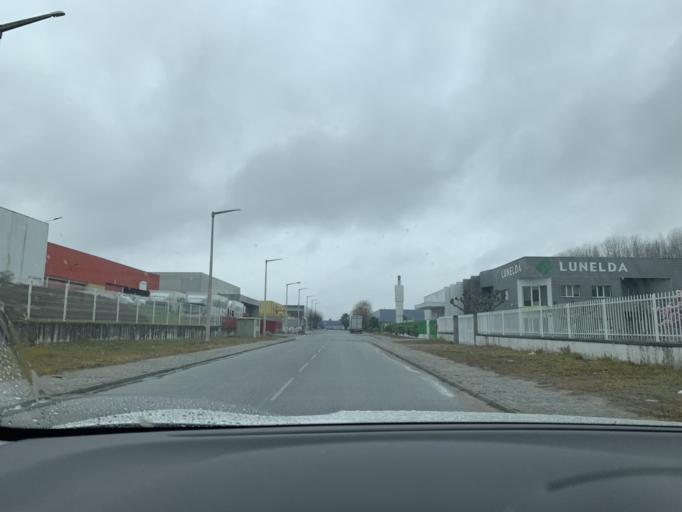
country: PT
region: Viseu
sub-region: Viseu
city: Rio de Loba
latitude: 40.6302
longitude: -7.8722
